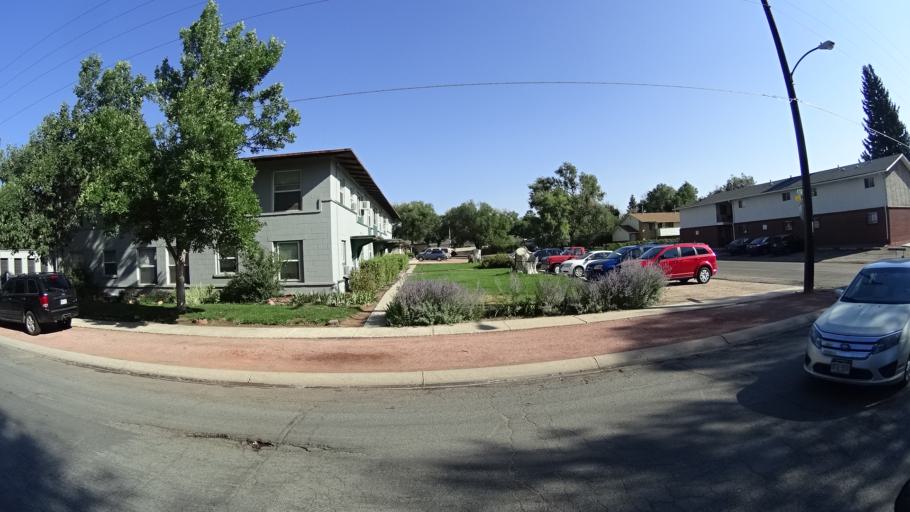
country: US
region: Colorado
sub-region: El Paso County
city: Colorado Springs
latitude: 38.8735
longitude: -104.8245
